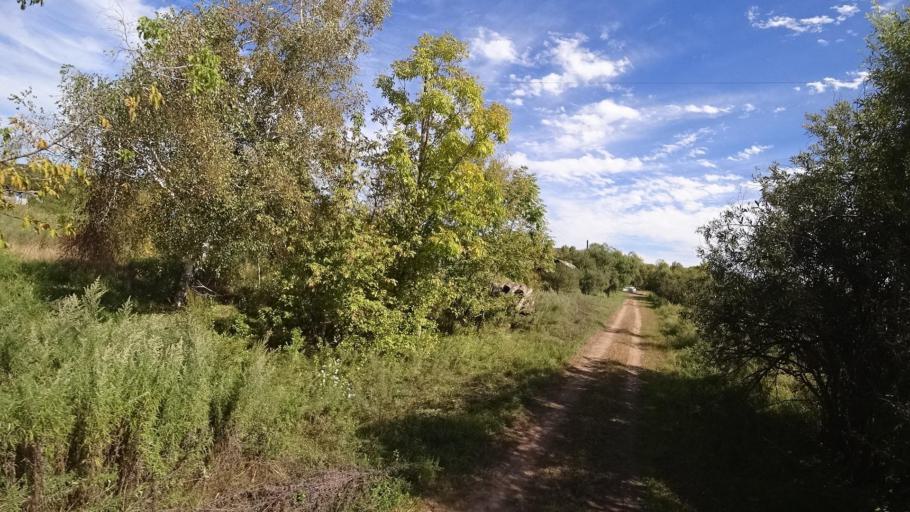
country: RU
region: Primorskiy
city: Yakovlevka
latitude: 44.4298
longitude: 133.5722
